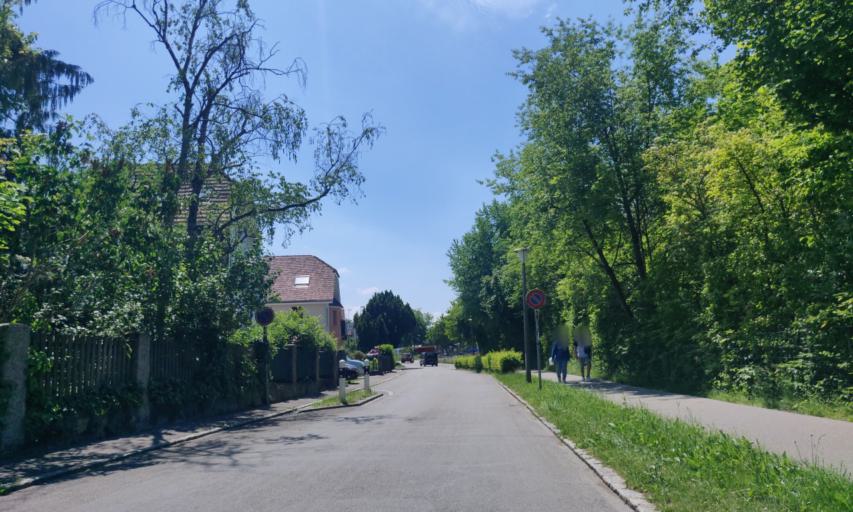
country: CH
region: Basel-Landschaft
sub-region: Bezirk Arlesheim
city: Munchenstein
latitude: 47.5246
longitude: 7.6180
